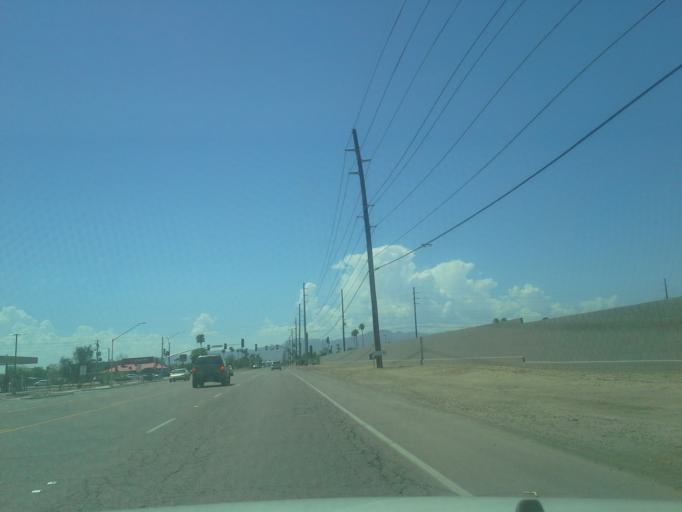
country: US
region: Arizona
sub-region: Maricopa County
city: Litchfield Park
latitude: 33.5368
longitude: -112.3390
